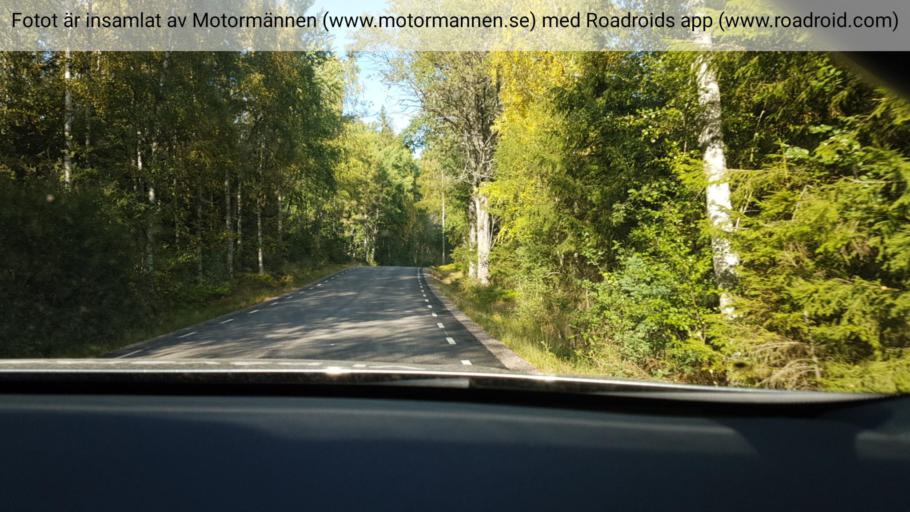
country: SE
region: Vaestra Goetaland
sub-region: Gotene Kommun
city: Goetene
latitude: 58.6348
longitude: 13.5387
